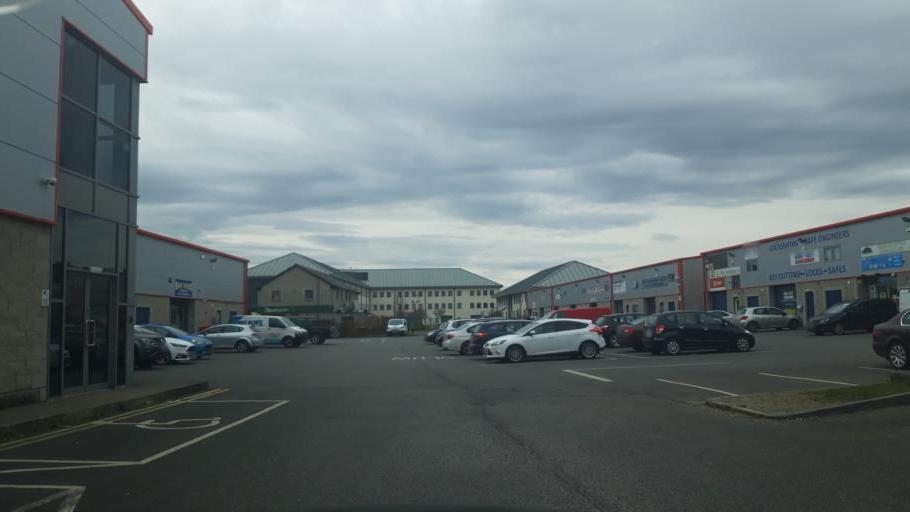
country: IE
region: Leinster
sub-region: Kildare
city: Celbridge
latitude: 53.3597
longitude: -6.5469
